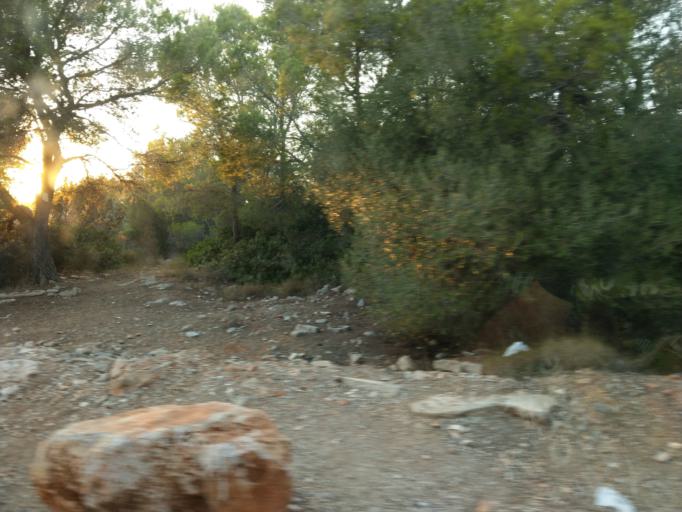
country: ES
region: Balearic Islands
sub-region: Illes Balears
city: Santanyi
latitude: 39.3136
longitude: 3.1197
